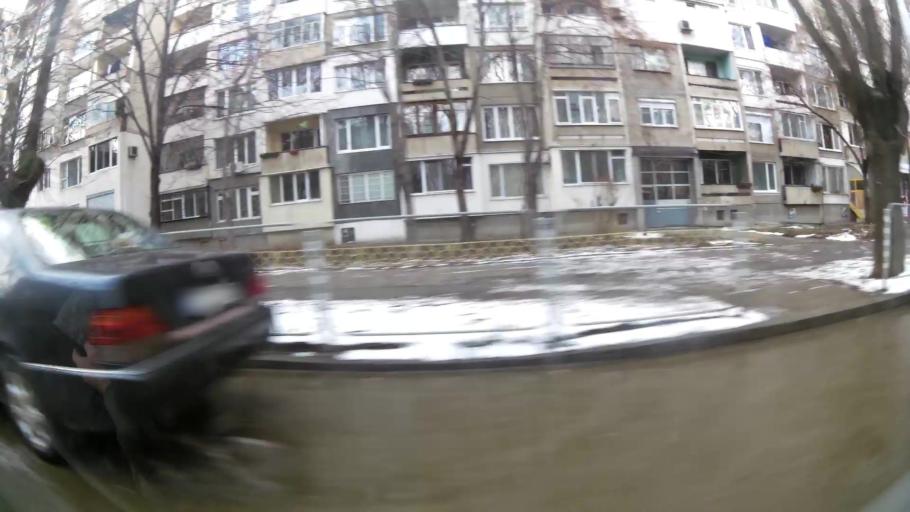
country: BG
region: Sofia-Capital
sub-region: Stolichna Obshtina
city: Sofia
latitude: 42.7070
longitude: 23.2917
